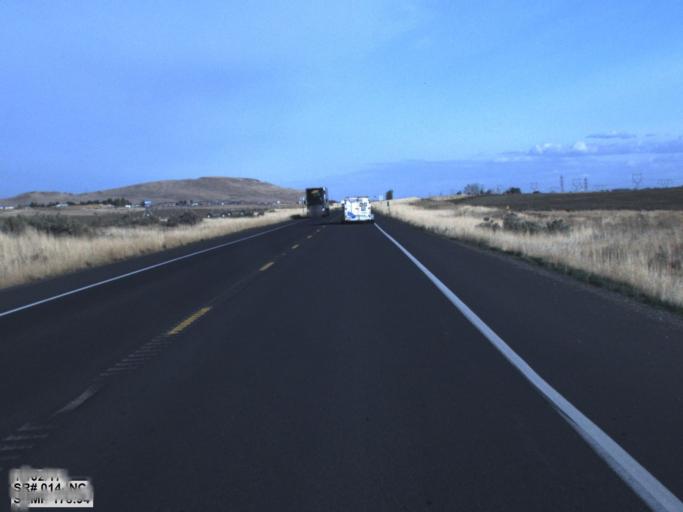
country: US
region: Oregon
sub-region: Umatilla County
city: Umatilla
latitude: 45.9466
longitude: -119.3723
